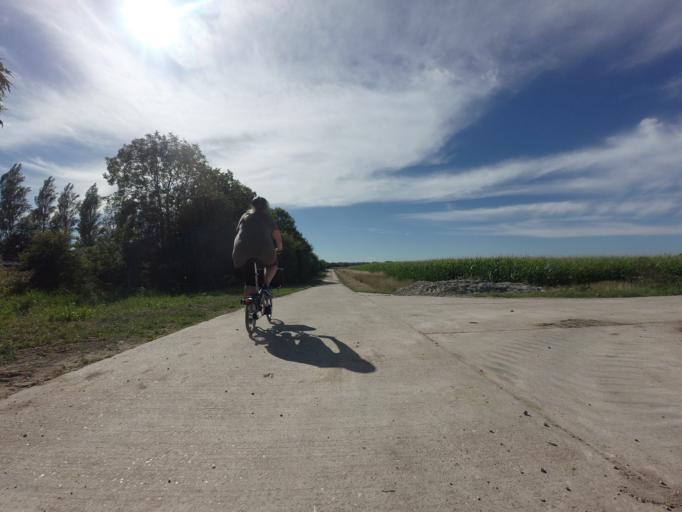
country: GB
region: England
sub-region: Kent
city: Herne Bay
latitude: 51.3638
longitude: 1.2107
